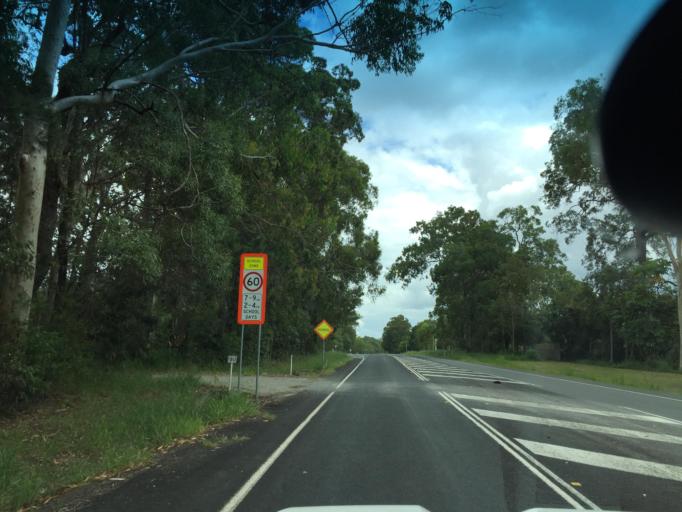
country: AU
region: Queensland
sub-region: Moreton Bay
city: Caboolture
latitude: -27.0567
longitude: 152.9406
